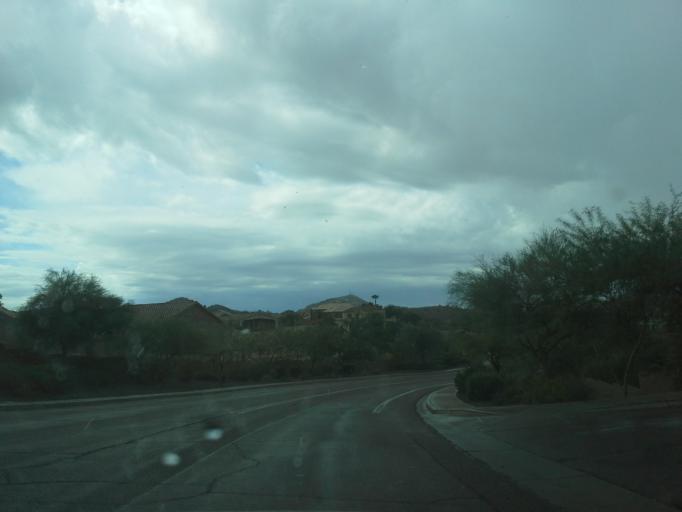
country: US
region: Arizona
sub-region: Maricopa County
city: Paradise Valley
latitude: 33.6106
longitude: -112.0525
